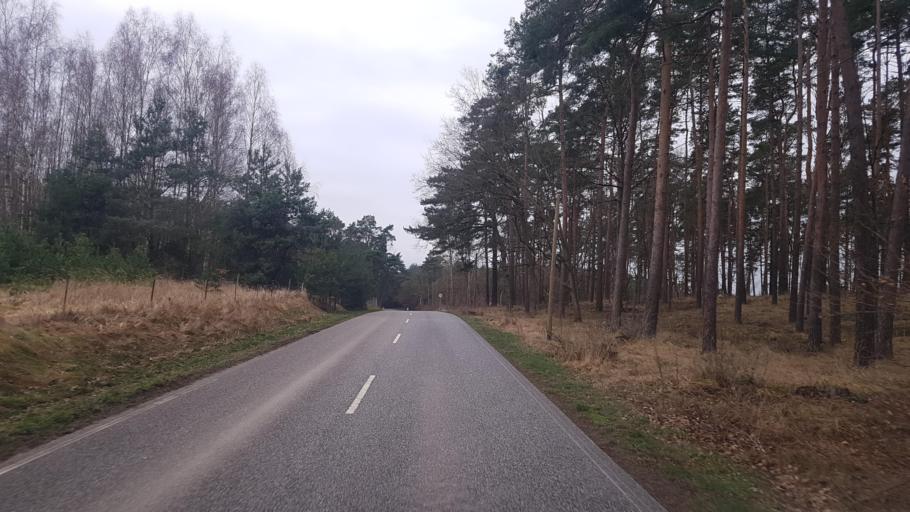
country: DE
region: Brandenburg
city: Oranienburg
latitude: 52.8493
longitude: 13.1585
